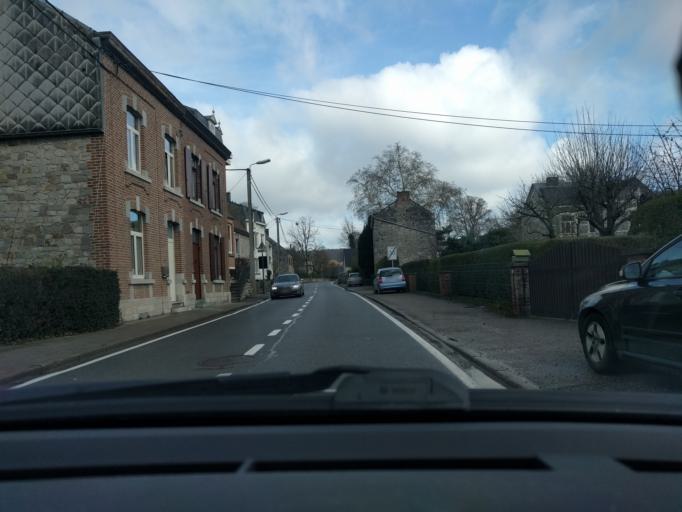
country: BE
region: Wallonia
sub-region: Province de Namur
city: Namur
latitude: 50.4692
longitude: 4.9252
